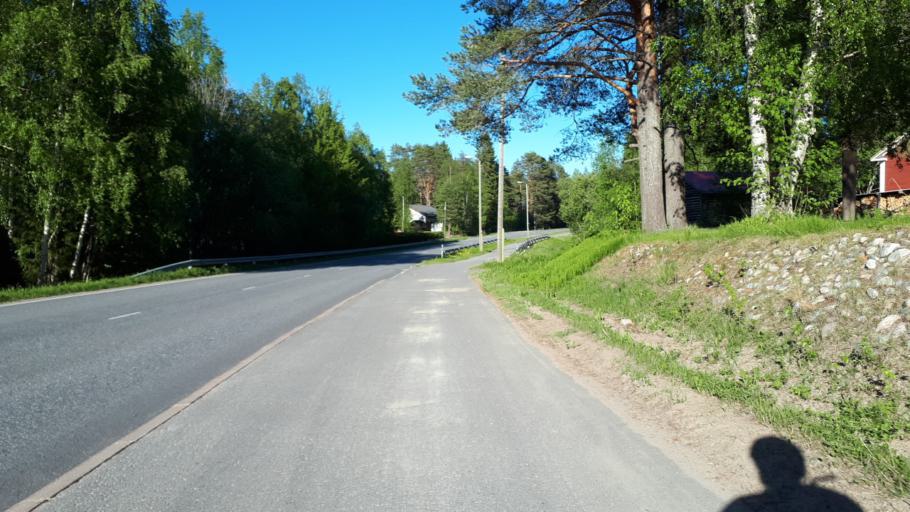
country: FI
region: Northern Ostrobothnia
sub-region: Oulunkaari
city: Ii
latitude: 65.3244
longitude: 25.4780
